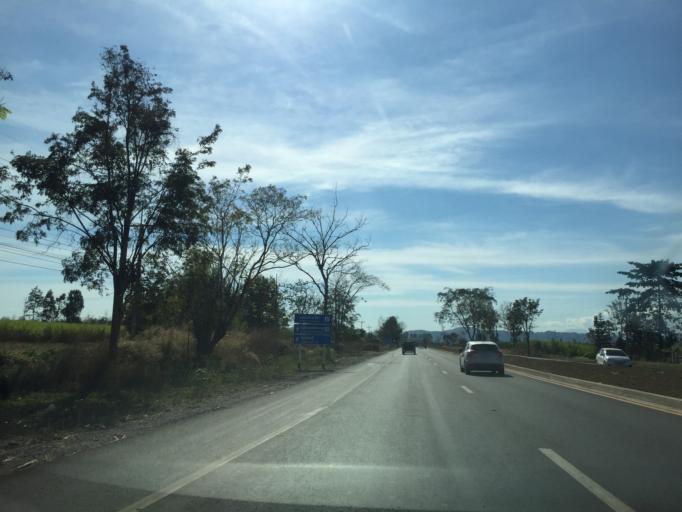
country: TH
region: Loei
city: Erawan
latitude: 17.3077
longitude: 101.8945
